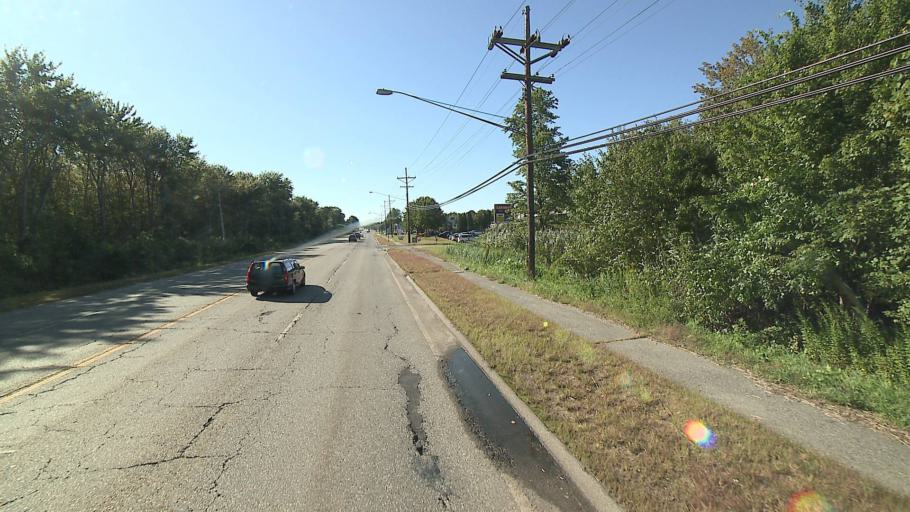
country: US
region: Connecticut
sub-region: New London County
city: Conning Towers-Nautilus Park
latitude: 41.3786
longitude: -72.0756
